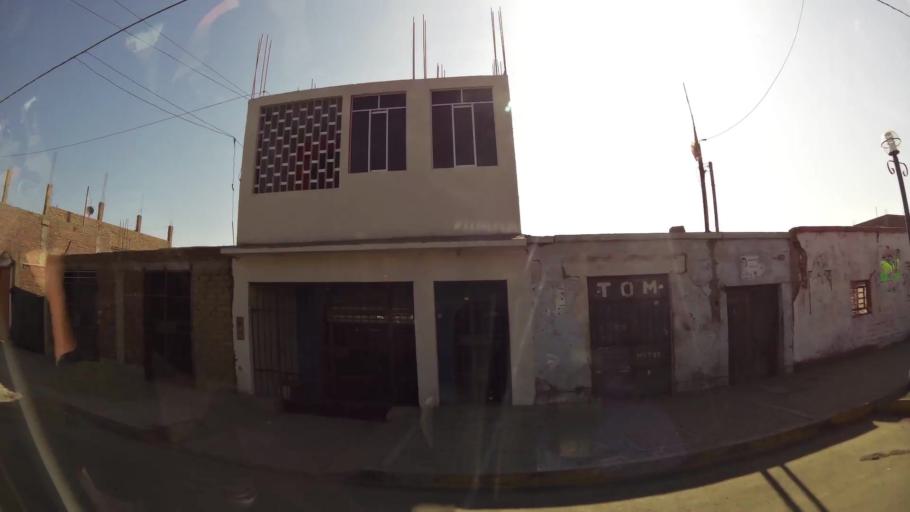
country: PE
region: Ica
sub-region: Provincia de Chincha
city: Chincha Alta
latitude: -13.4008
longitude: -76.1288
